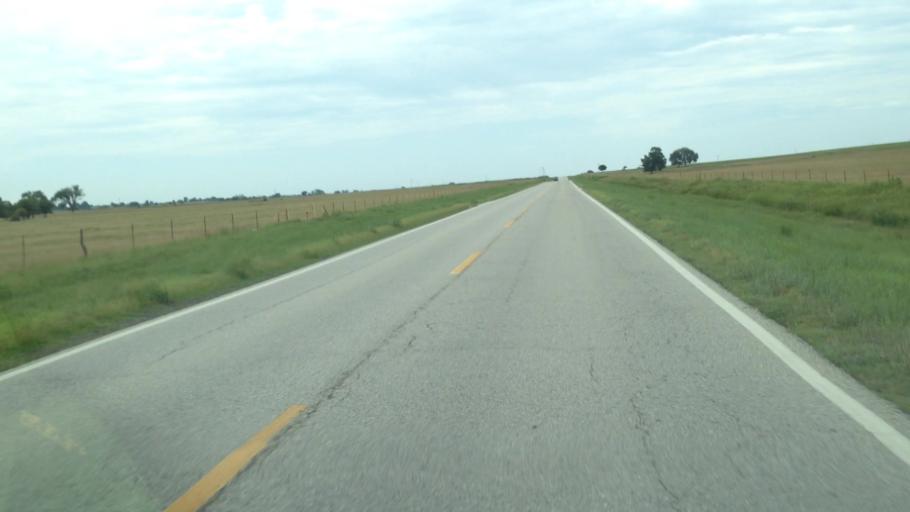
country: US
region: Oklahoma
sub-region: Craig County
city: Vinita
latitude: 36.8383
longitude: -95.1304
